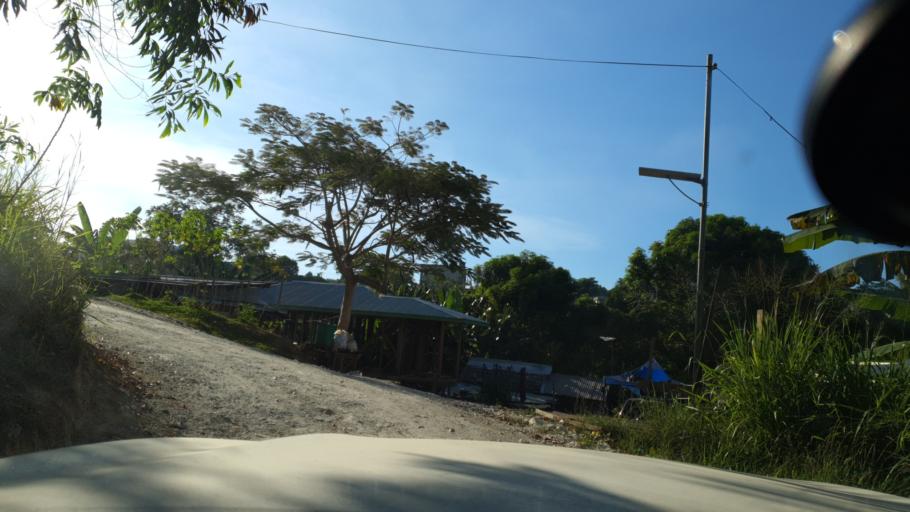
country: SB
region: Guadalcanal
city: Honiara
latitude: -9.4337
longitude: 160.0051
